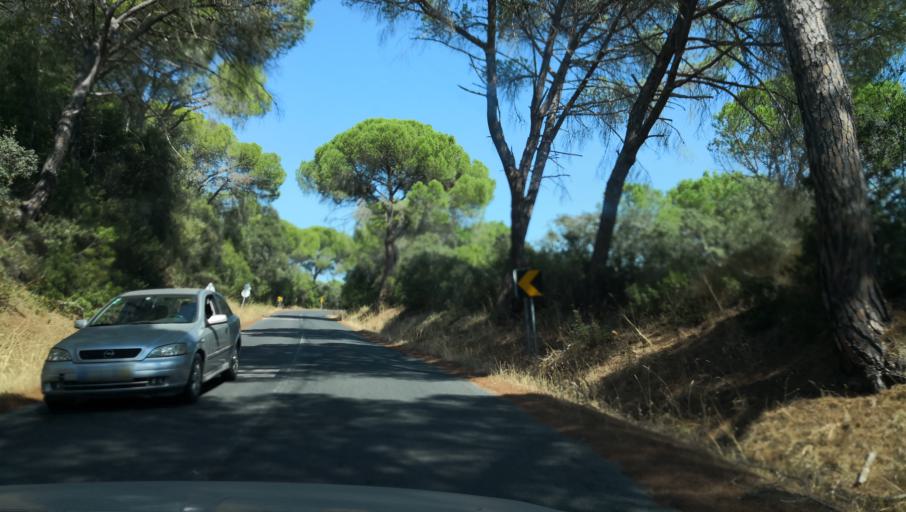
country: PT
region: Setubal
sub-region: Alcacer do Sal
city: Alcacer do Sal
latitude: 38.2889
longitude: -8.4044
